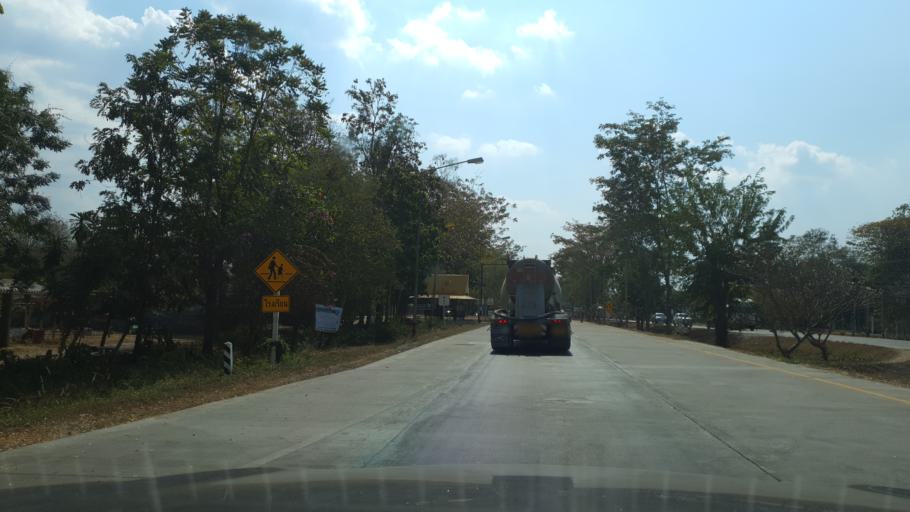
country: TH
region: Lampang
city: Mae Phrik
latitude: 17.4456
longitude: 99.1594
